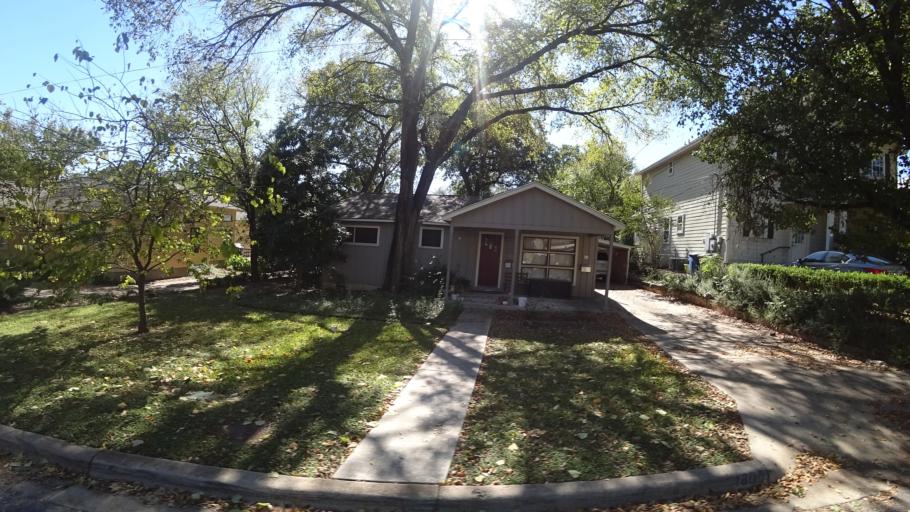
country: US
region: Texas
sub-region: Travis County
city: Austin
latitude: 30.2828
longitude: -97.7631
